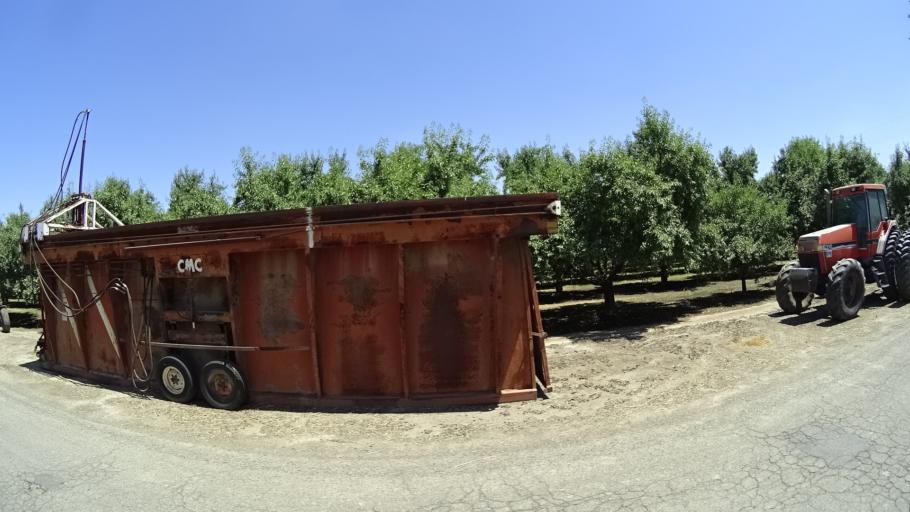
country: US
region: California
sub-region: Kings County
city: Lucerne
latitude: 36.4090
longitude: -119.6010
